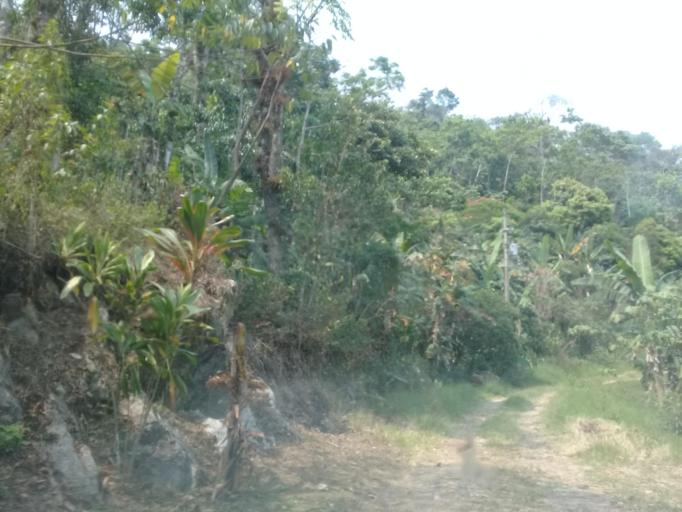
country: MX
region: Veracruz
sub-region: Tezonapa
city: Laguna Chica (Pueblo Nuevo)
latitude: 18.5843
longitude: -96.7490
